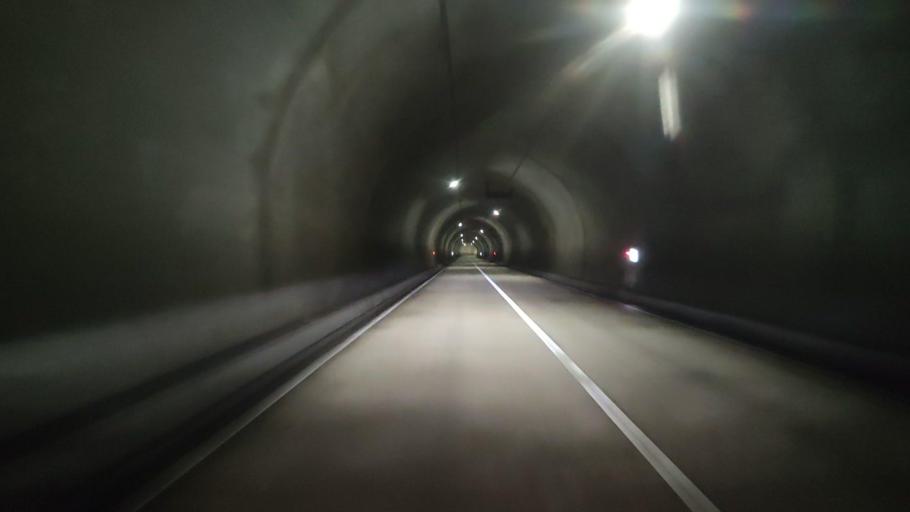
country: JP
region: Wakayama
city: Shingu
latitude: 33.8759
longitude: 135.8579
